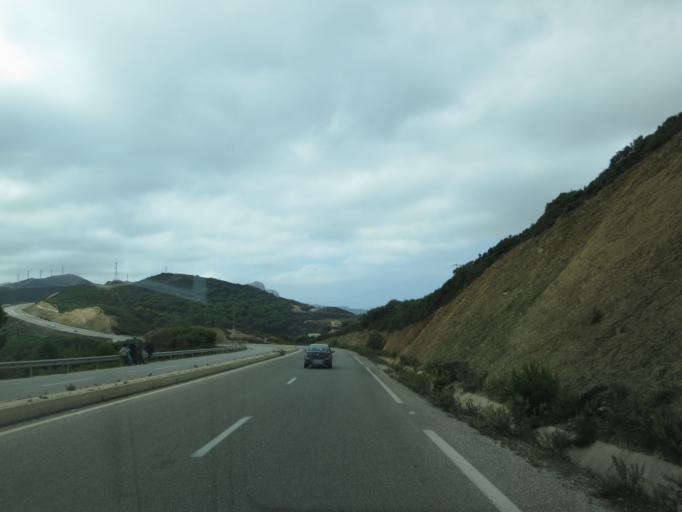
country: ES
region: Ceuta
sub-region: Ceuta
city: Ceuta
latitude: 35.8642
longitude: -5.4177
